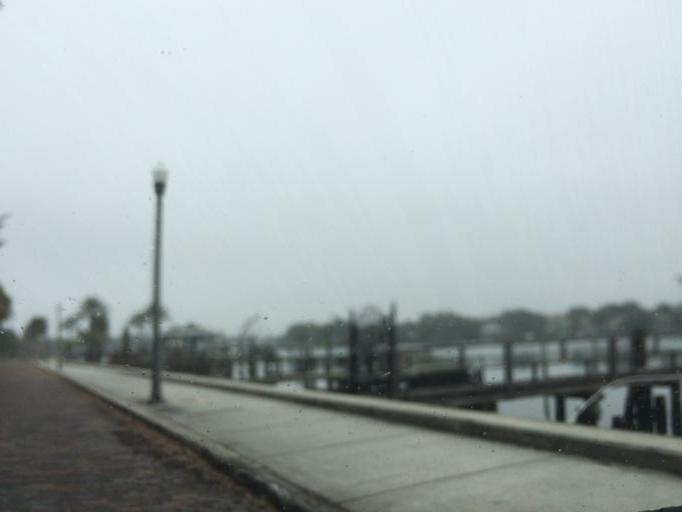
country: US
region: Florida
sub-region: Pinellas County
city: Saint Petersburg
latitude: 27.7929
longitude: -82.6305
